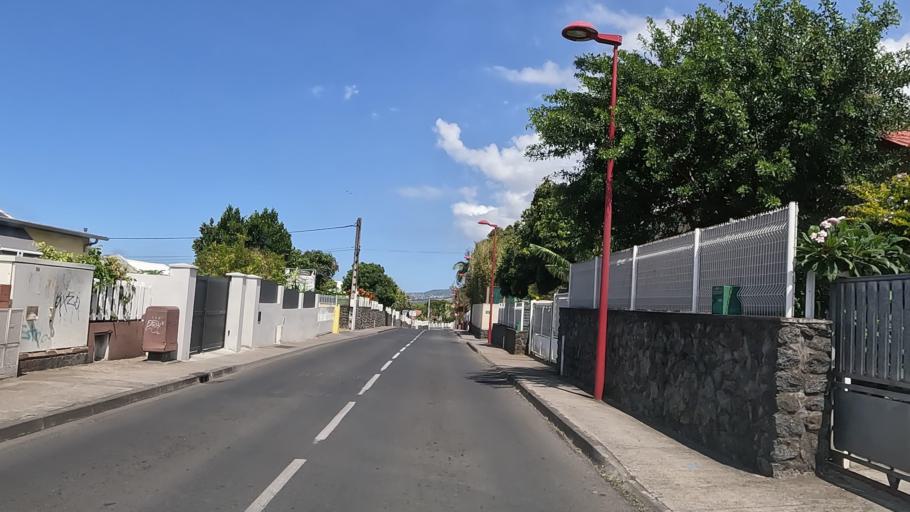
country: RE
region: Reunion
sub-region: Reunion
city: Saint-Louis
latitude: -21.2770
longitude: 55.4449
